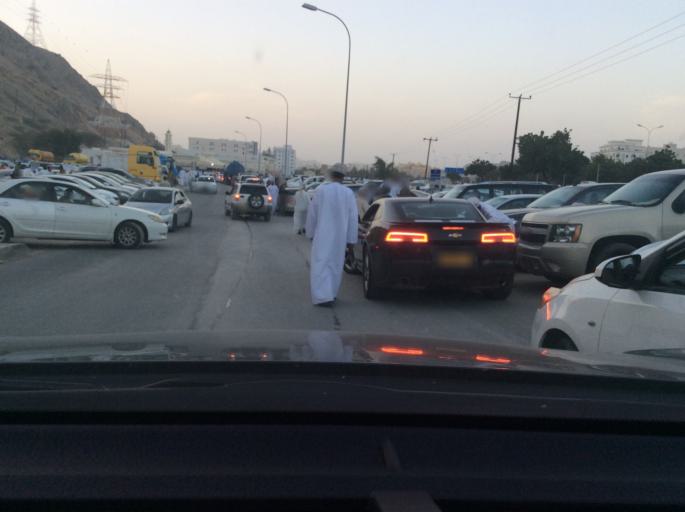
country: OM
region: Muhafazat Masqat
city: Muscat
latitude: 23.5769
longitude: 58.5640
